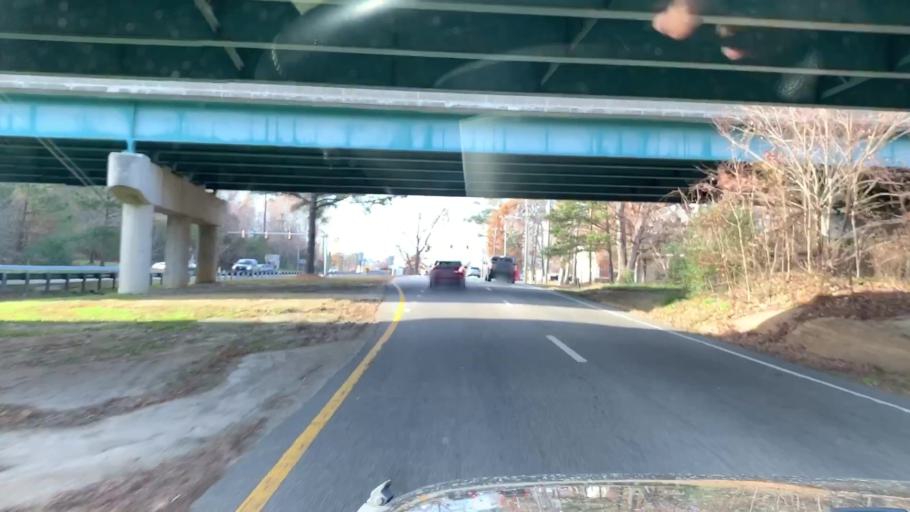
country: US
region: Virginia
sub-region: James City County
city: Williamsburg
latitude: 37.3365
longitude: -76.7501
